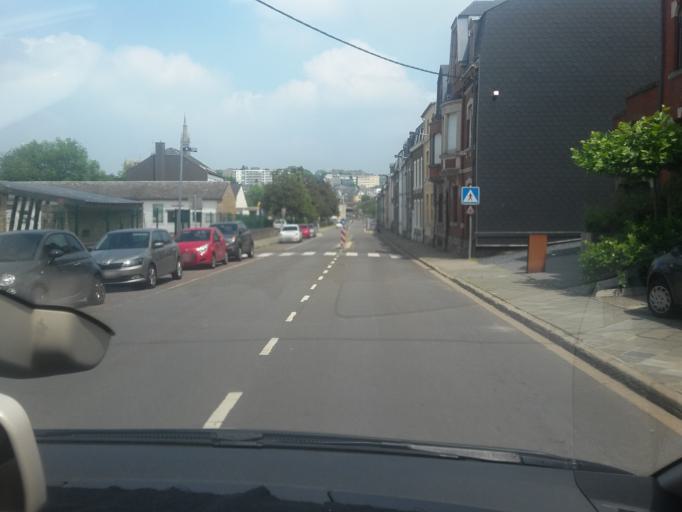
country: BE
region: Wallonia
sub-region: Province du Luxembourg
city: Arlon
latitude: 49.6753
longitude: 5.8105
